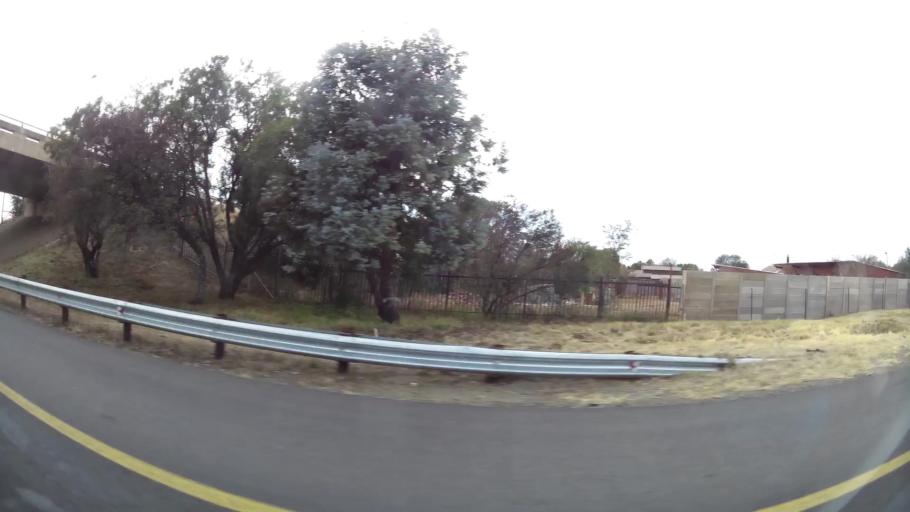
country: ZA
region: Orange Free State
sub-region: Mangaung Metropolitan Municipality
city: Bloemfontein
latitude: -29.1451
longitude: 26.1712
